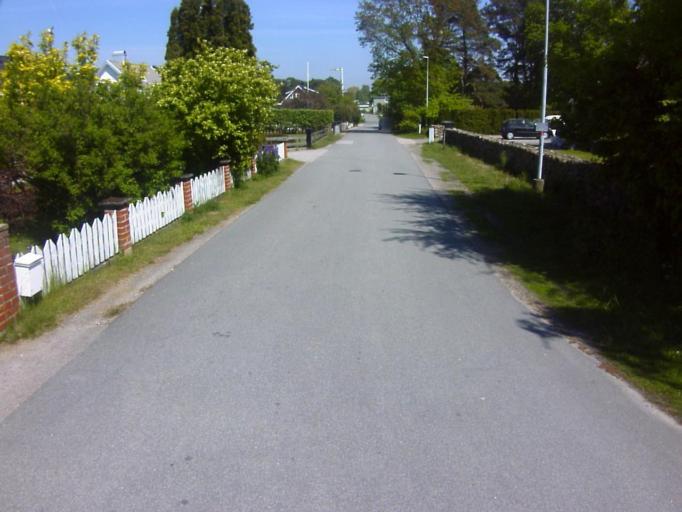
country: SE
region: Blekinge
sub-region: Solvesborgs Kommun
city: Soelvesborg
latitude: 56.0150
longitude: 14.6983
